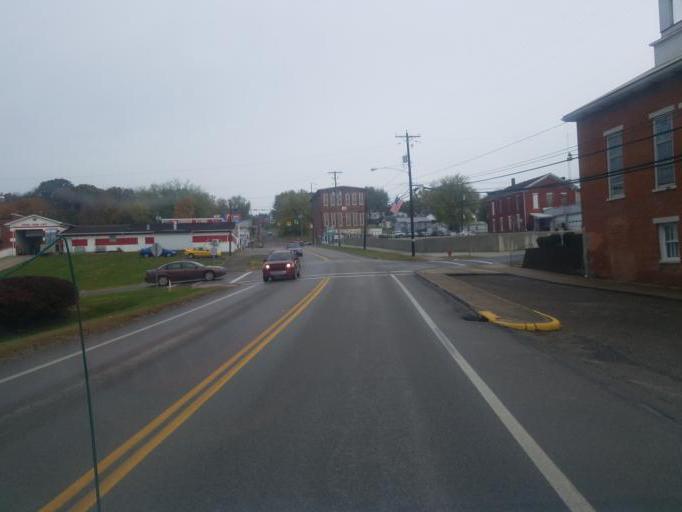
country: US
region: Ohio
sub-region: Washington County
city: Beverly
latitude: 39.5467
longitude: -81.6402
